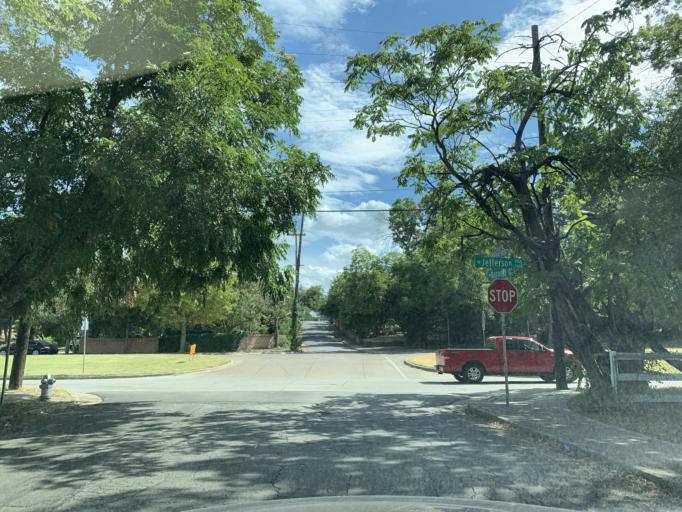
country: US
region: Texas
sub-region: Dallas County
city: Cockrell Hill
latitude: 32.7448
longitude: -96.8714
